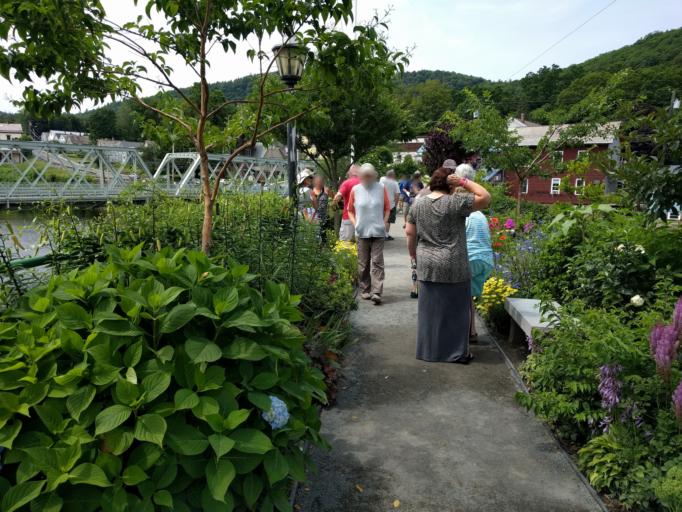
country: US
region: Massachusetts
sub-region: Franklin County
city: Shelburne Falls
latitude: 42.6041
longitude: -72.7404
